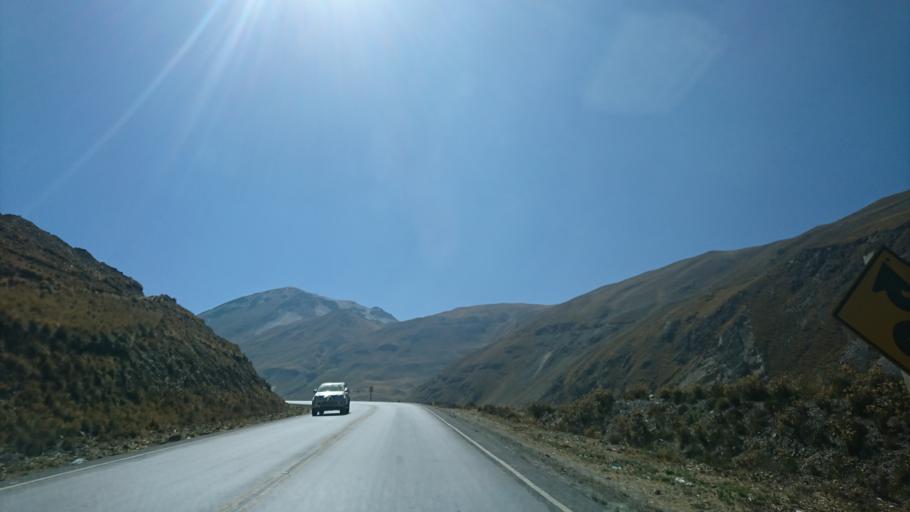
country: BO
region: La Paz
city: La Paz
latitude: -16.4273
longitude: -68.0625
